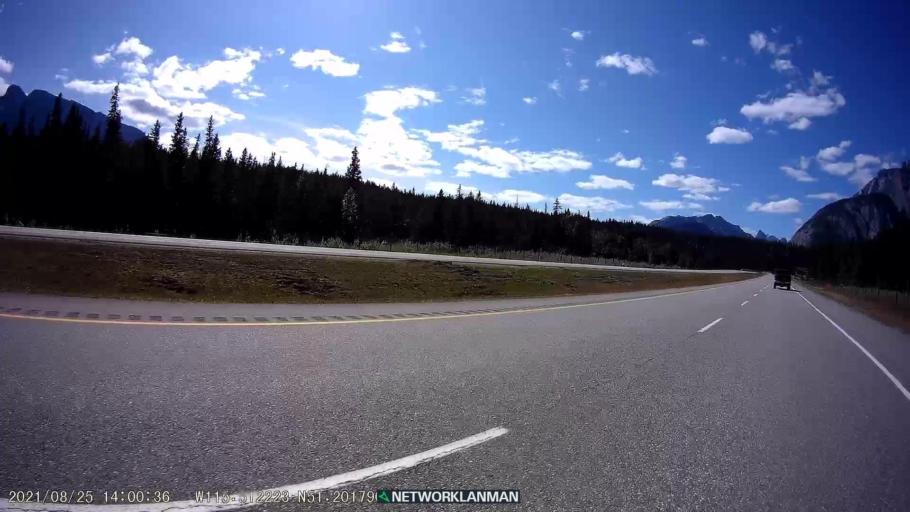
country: CA
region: Alberta
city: Banff
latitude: 51.2007
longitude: -115.5127
